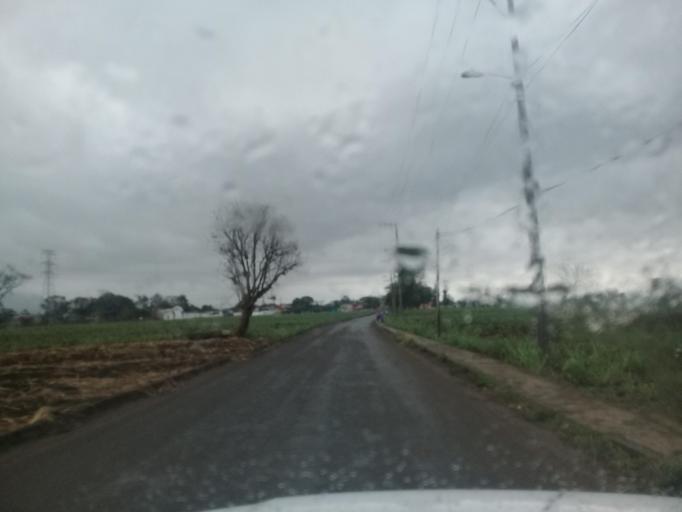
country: MX
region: Veracruz
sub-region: Amatlan de los Reyes
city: Trapiche Viejo
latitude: 18.8445
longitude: -96.9468
